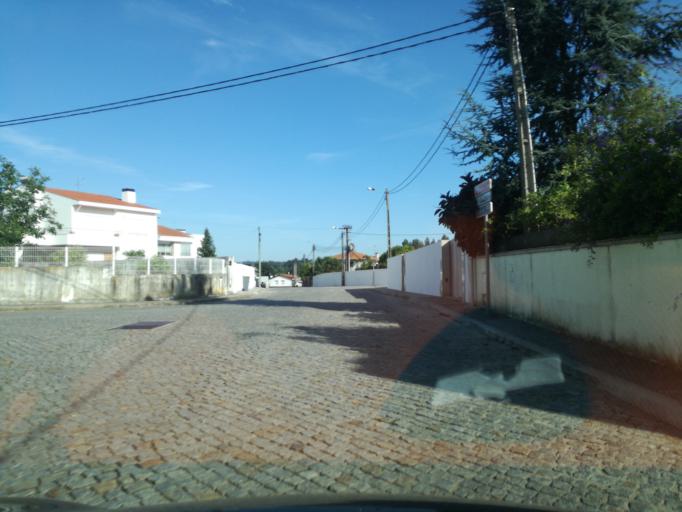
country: PT
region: Porto
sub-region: Maia
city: Nogueira
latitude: 41.2623
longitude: -8.5976
